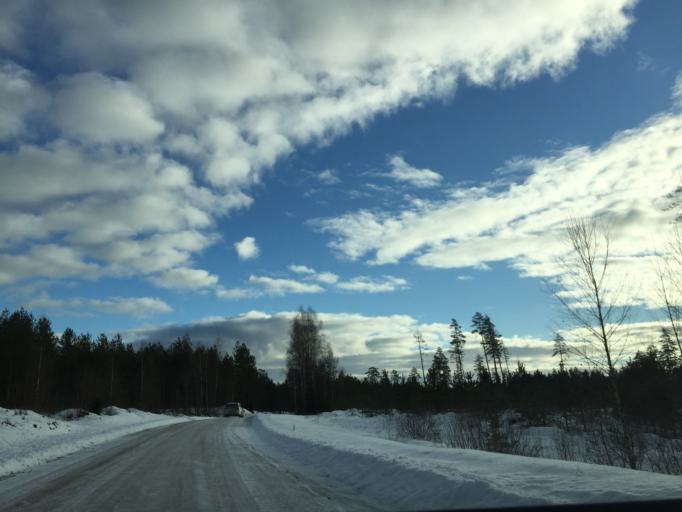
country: LV
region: Lielvarde
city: Lielvarde
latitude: 56.5653
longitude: 24.8321
